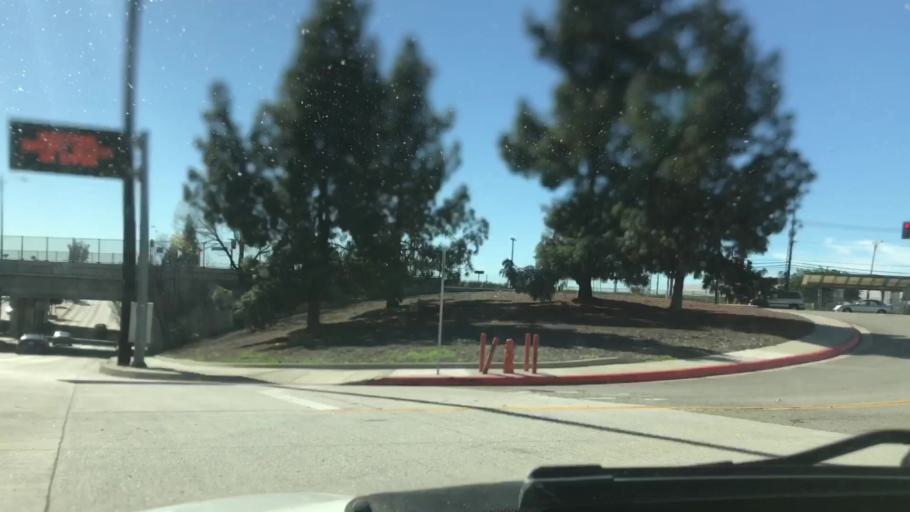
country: US
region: California
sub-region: Los Angeles County
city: North Hollywood
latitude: 34.2066
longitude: -118.3488
